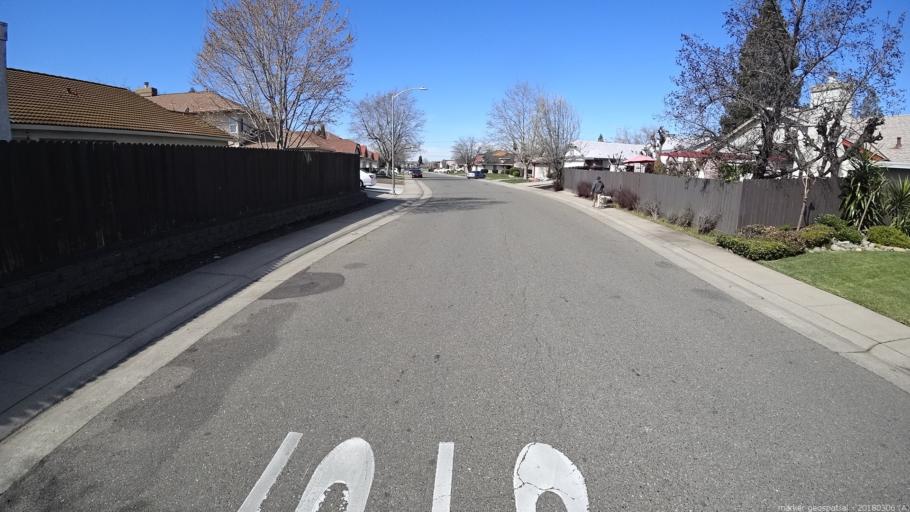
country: US
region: California
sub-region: Sacramento County
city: Vineyard
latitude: 38.4616
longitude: -121.3482
